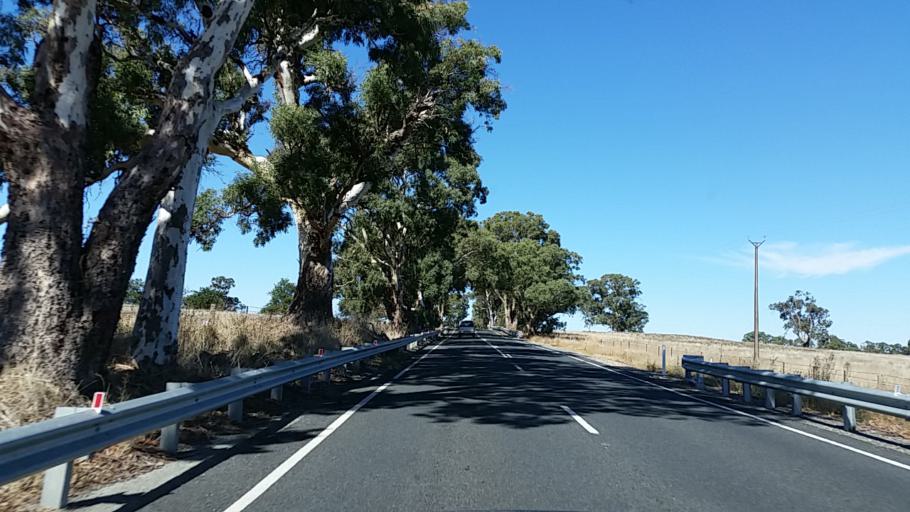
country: AU
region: South Australia
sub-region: Adelaide Hills
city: Birdwood
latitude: -34.7710
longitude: 139.0251
